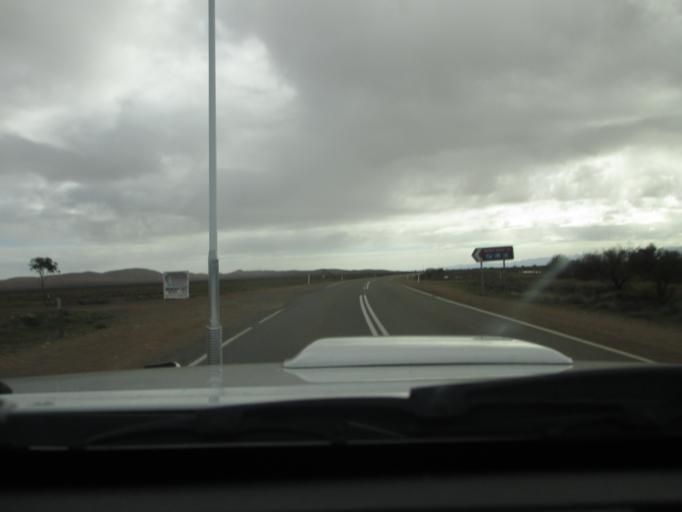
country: AU
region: South Australia
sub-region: Flinders Ranges
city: Quorn
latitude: -31.5454
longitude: 138.4243
